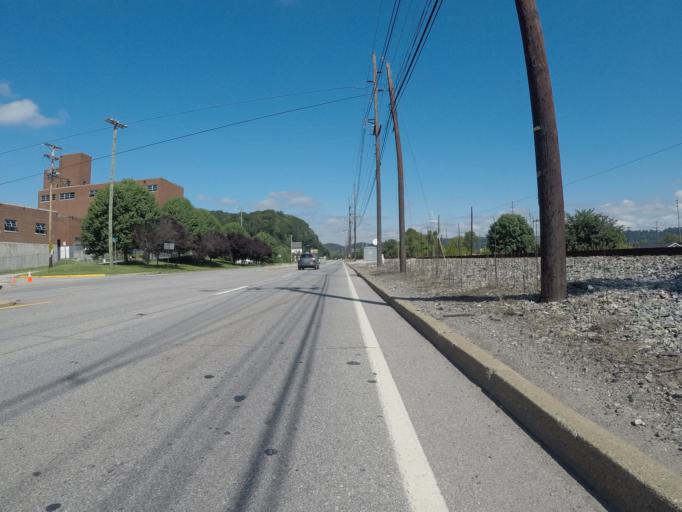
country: US
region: Kentucky
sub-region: Boyd County
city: Ashland
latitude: 38.4529
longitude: -82.6124
